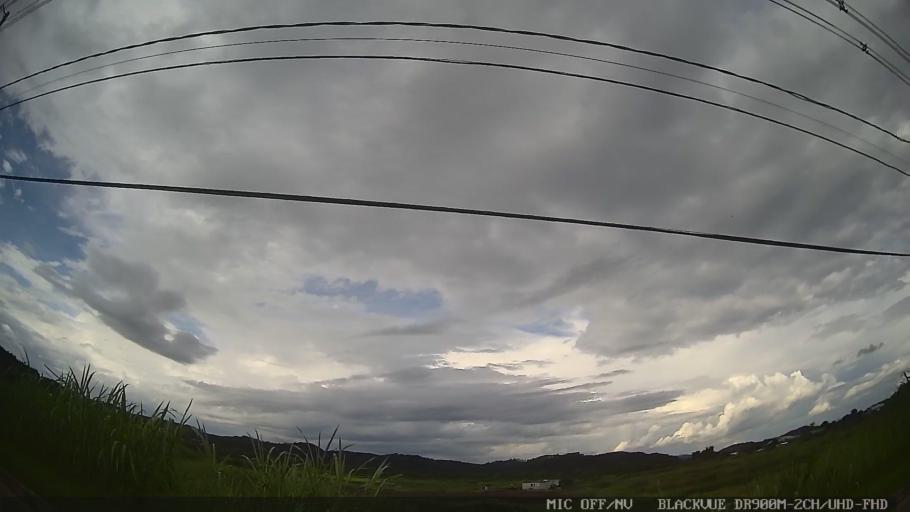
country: BR
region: Sao Paulo
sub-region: Biritiba-Mirim
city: Biritiba Mirim
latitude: -23.5668
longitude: -46.0741
